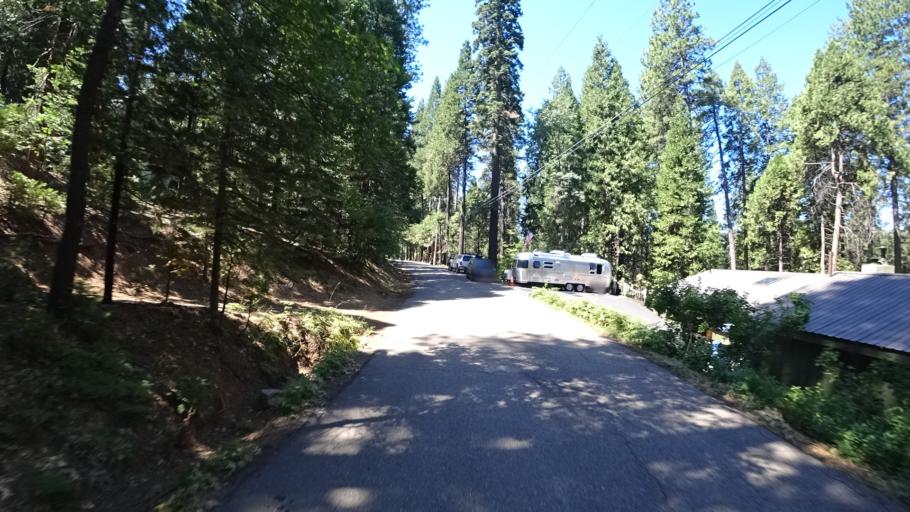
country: US
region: California
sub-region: Calaveras County
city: Arnold
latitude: 38.2312
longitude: -120.3747
